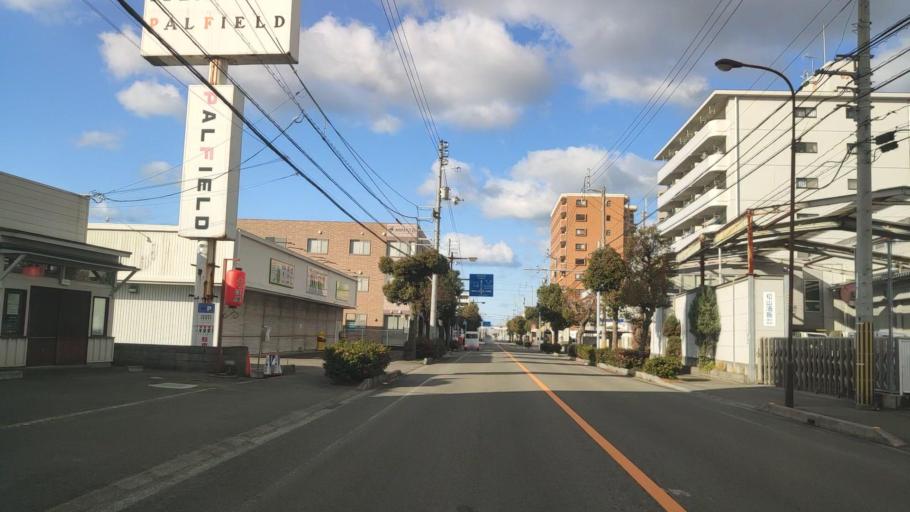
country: JP
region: Ehime
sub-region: Shikoku-chuo Shi
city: Matsuyama
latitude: 33.8286
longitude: 132.7477
